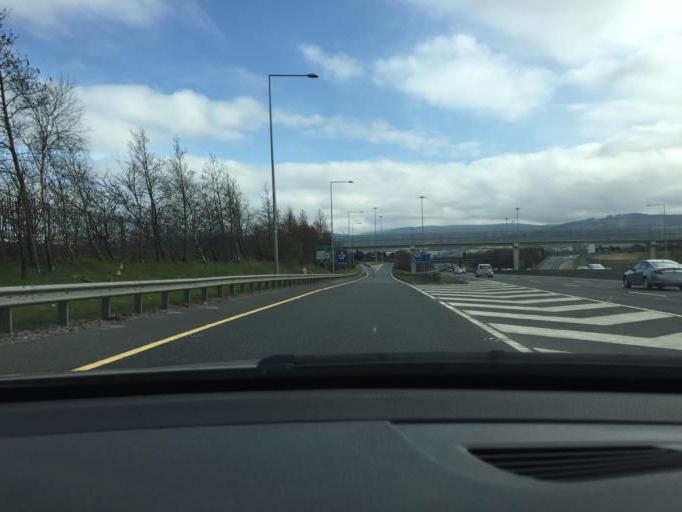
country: IE
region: Leinster
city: Firhouse
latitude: 53.2953
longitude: -6.3333
